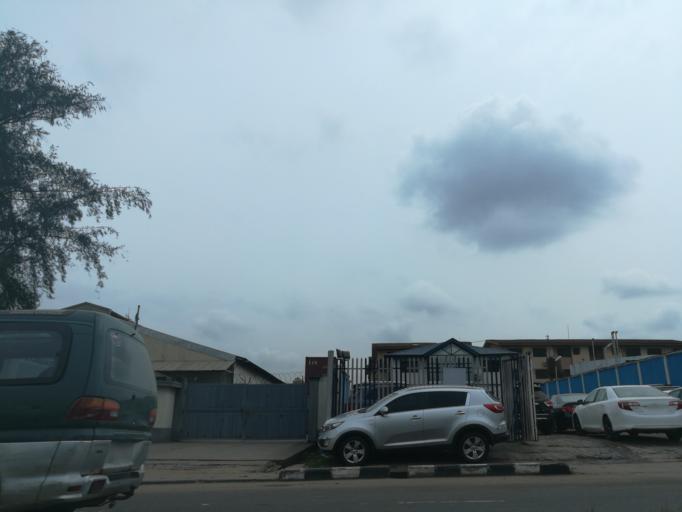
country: NG
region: Lagos
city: Ojota
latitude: 6.5915
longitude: 3.3736
